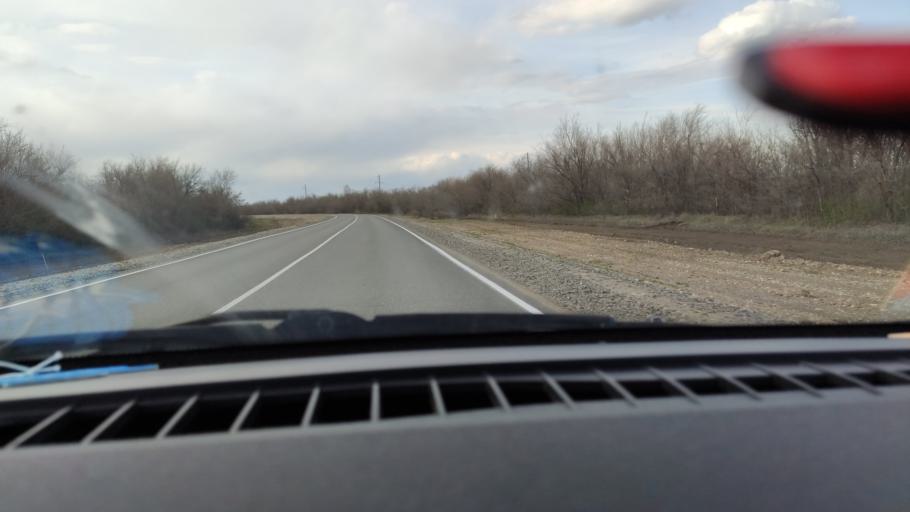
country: RU
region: Saratov
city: Privolzhskiy
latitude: 51.1591
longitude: 45.9589
